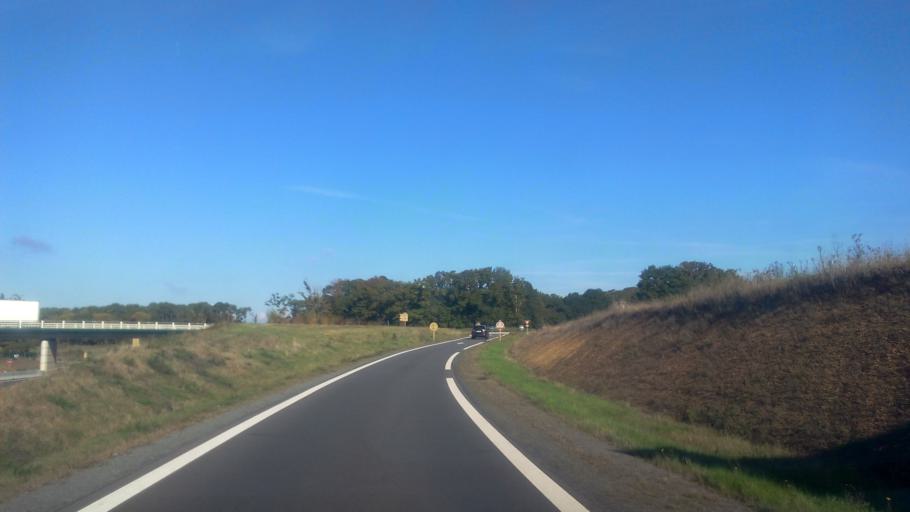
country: FR
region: Brittany
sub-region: Departement d'Ille-et-Vilaine
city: Bains-sur-Oust
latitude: 47.6758
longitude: -2.0622
